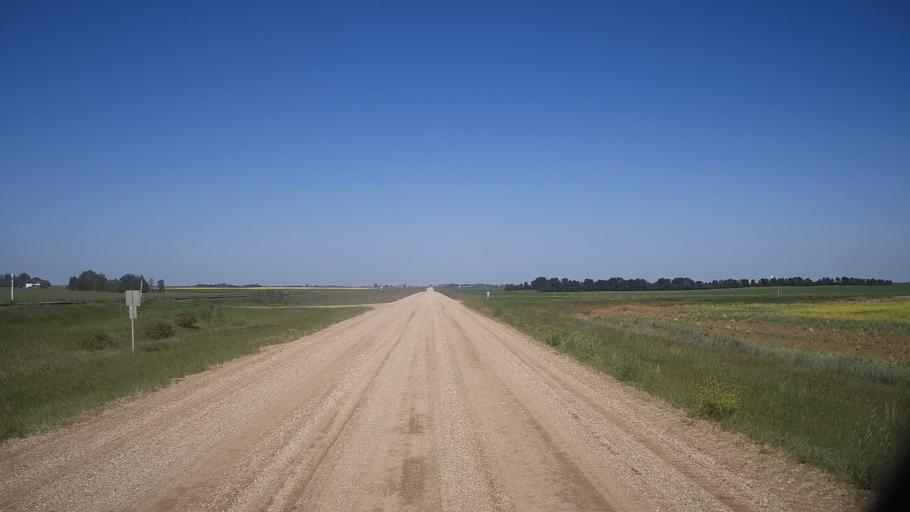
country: CA
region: Saskatchewan
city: Watrous
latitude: 51.8742
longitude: -106.0028
